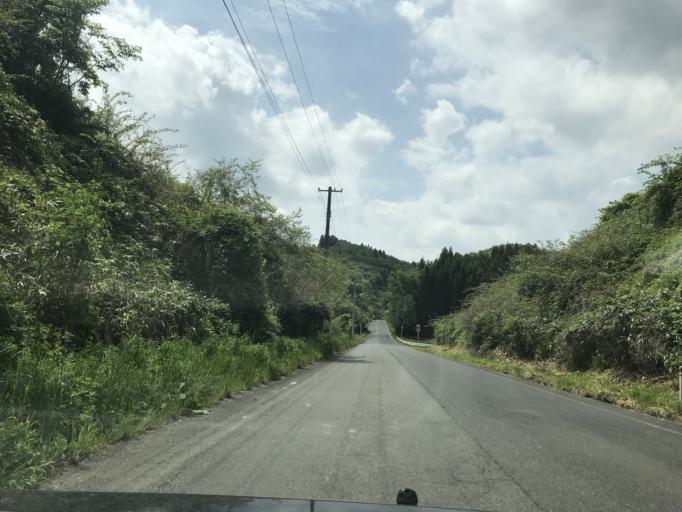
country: JP
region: Miyagi
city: Furukawa
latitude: 38.7584
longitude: 140.9390
